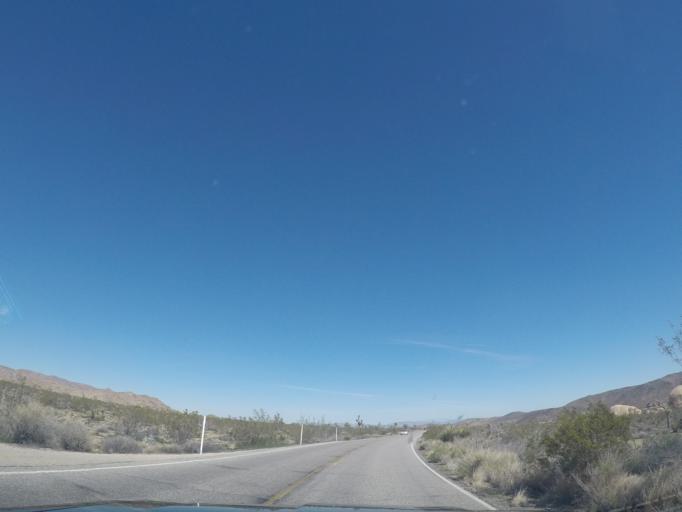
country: US
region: California
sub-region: San Bernardino County
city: Twentynine Palms
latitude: 33.9994
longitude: -116.0237
